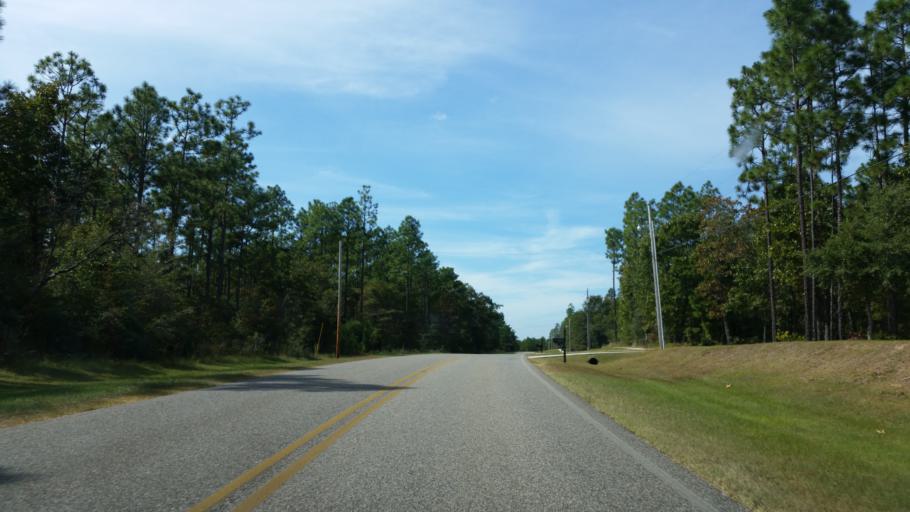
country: US
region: Alabama
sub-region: Baldwin County
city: Spanish Fort
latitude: 30.7362
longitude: -87.8502
